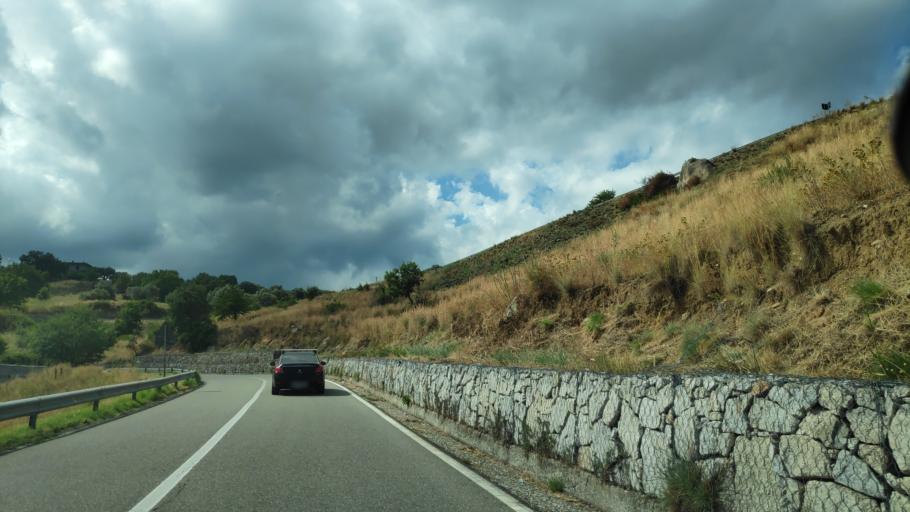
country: IT
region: Calabria
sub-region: Provincia di Catanzaro
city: Santa Caterina dello Ionio
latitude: 38.5244
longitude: 16.5342
